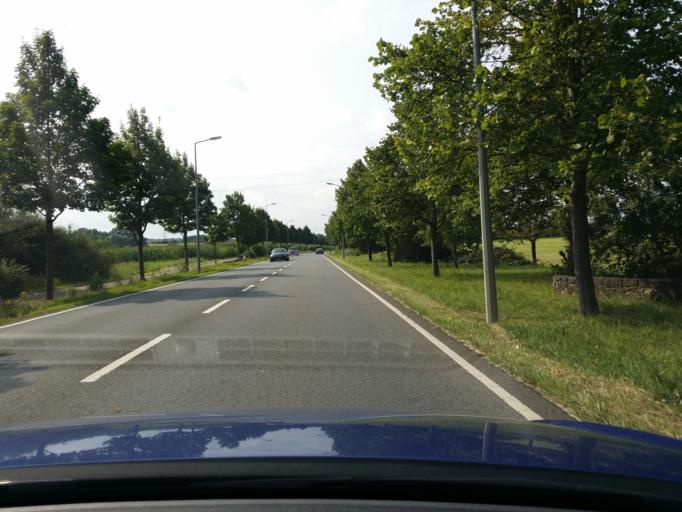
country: LU
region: Luxembourg
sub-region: Canton de Luxembourg
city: Bertrange
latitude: 49.6054
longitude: 6.0589
